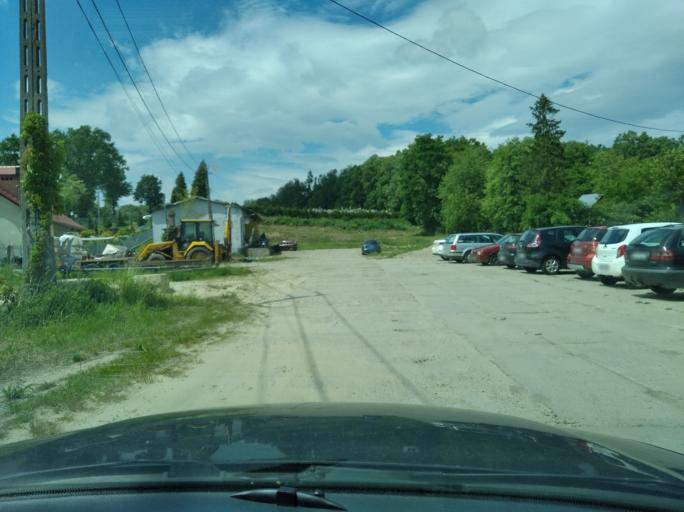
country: PL
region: Subcarpathian Voivodeship
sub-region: Powiat ropczycko-sedziszowski
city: Ropczyce
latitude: 50.0553
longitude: 21.6104
